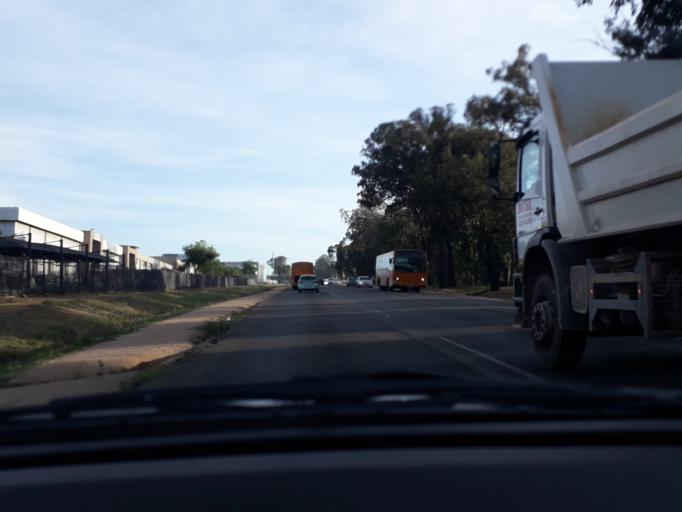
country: ZA
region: Gauteng
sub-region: City of Johannesburg Metropolitan Municipality
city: Midrand
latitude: -25.9462
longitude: 28.1430
